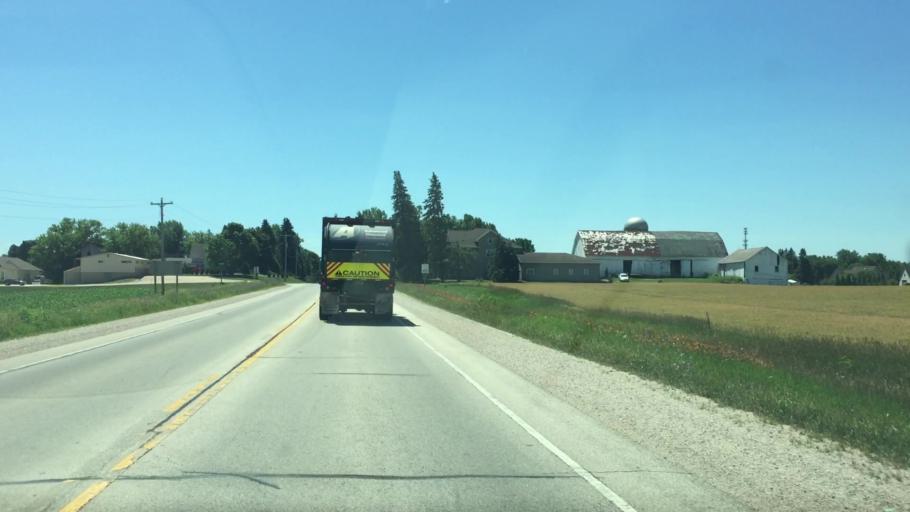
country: US
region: Wisconsin
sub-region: Calumet County
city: Chilton
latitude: 44.0439
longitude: -88.1630
